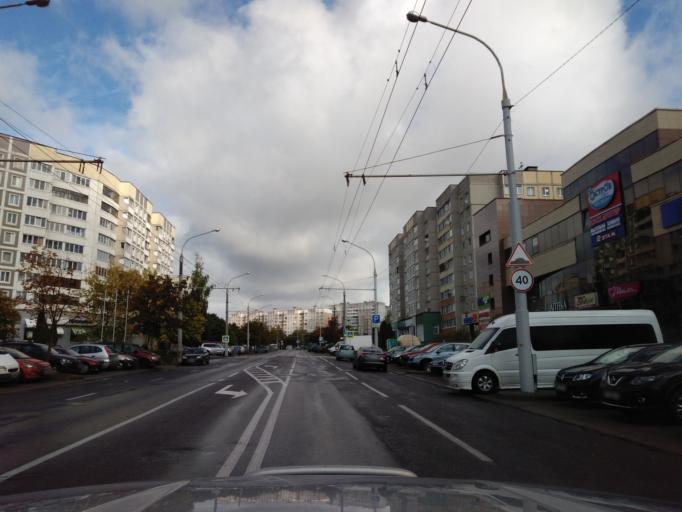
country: BY
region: Minsk
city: Novoye Medvezhino
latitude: 53.8833
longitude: 27.4389
